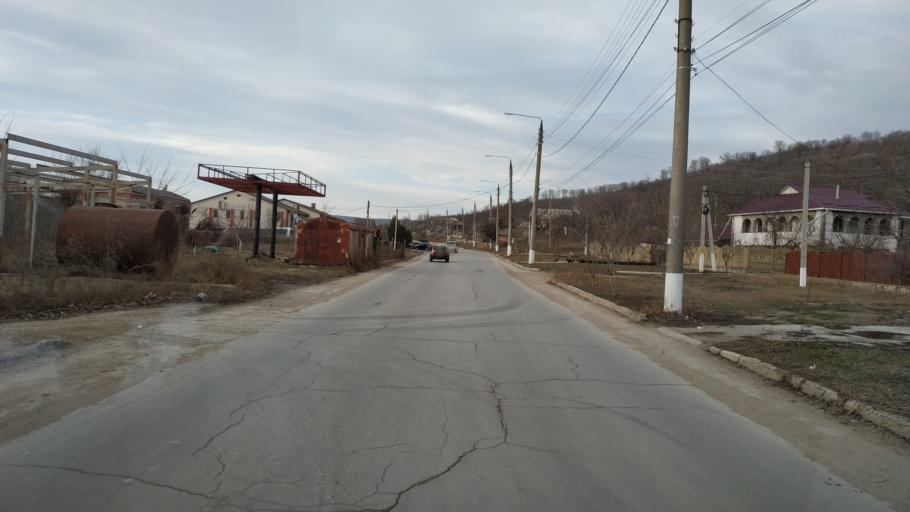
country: MD
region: Nisporeni
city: Nisporeni
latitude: 47.0862
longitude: 28.1824
